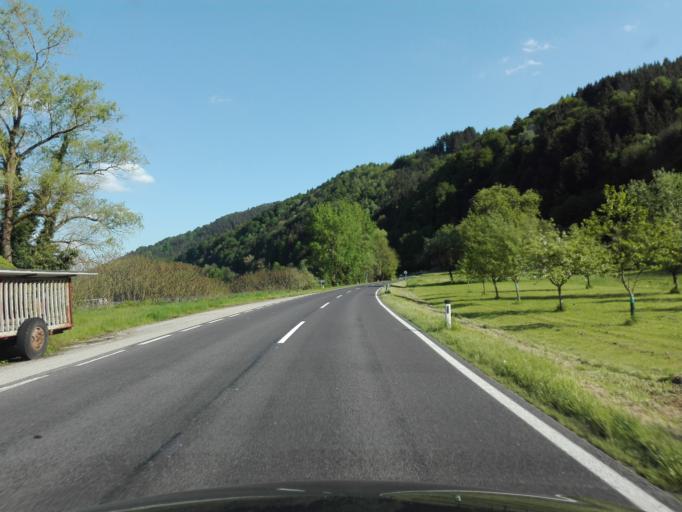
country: AT
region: Upper Austria
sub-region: Politischer Bezirk Rohrbach
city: Pfarrkirchen im Muehlkreis
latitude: 48.4712
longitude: 13.7737
